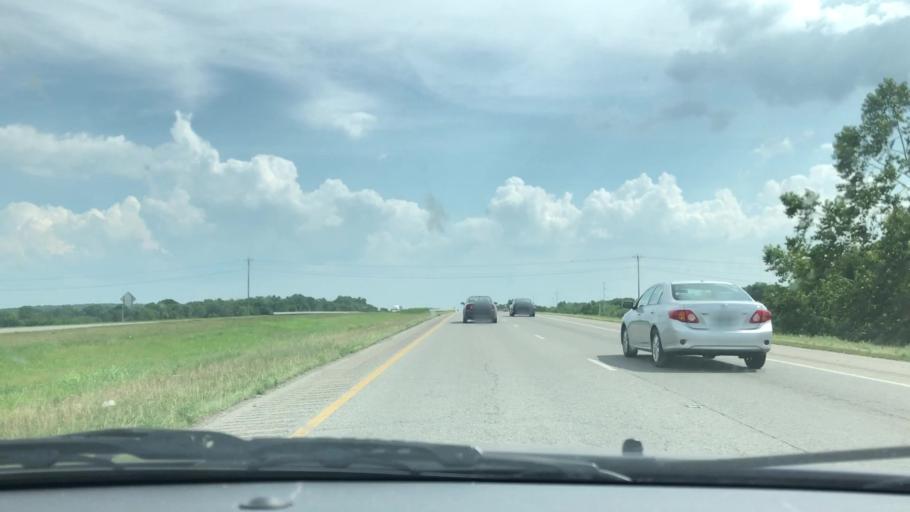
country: US
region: Tennessee
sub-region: Wilson County
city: Rural Hill
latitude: 36.1143
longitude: -86.4087
